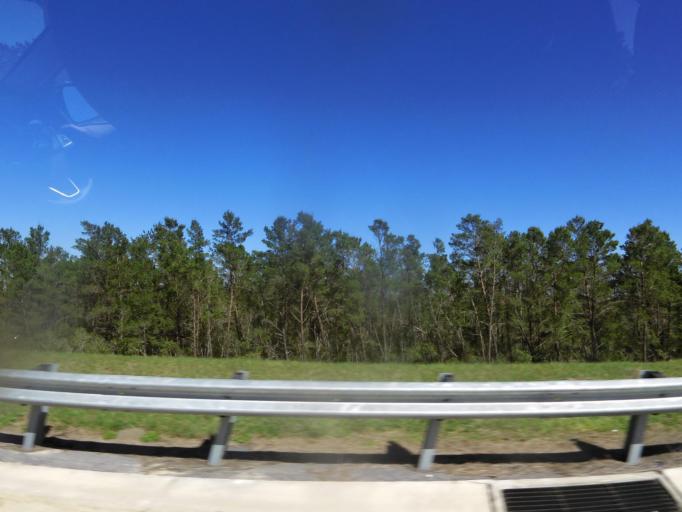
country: US
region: Florida
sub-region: Lake County
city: Mount Plymouth
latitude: 28.7867
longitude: -81.5742
